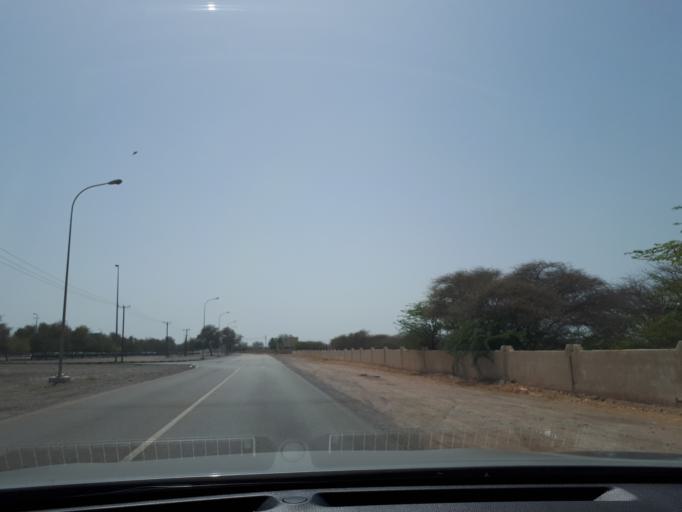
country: OM
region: Al Batinah
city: Barka'
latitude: 23.6904
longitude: 58.0374
